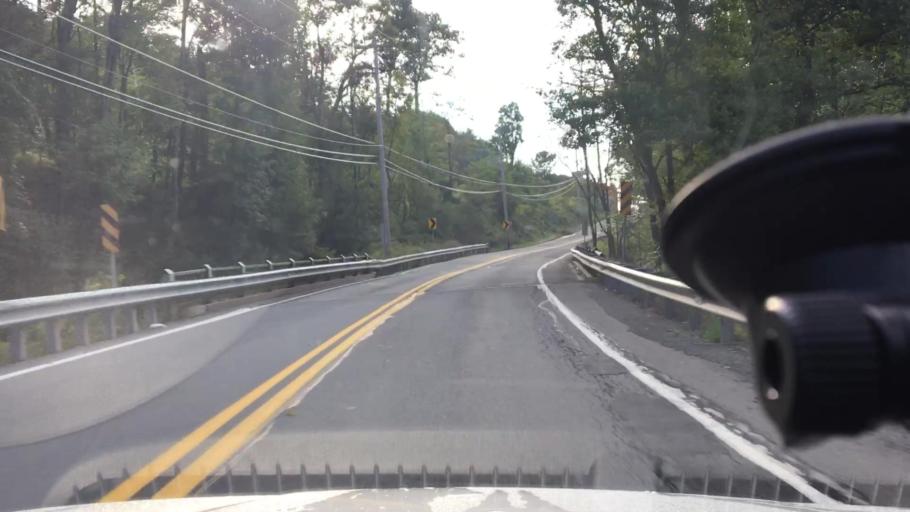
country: US
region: Pennsylvania
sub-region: Monroe County
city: Mount Pocono
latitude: 41.0981
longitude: -75.3339
